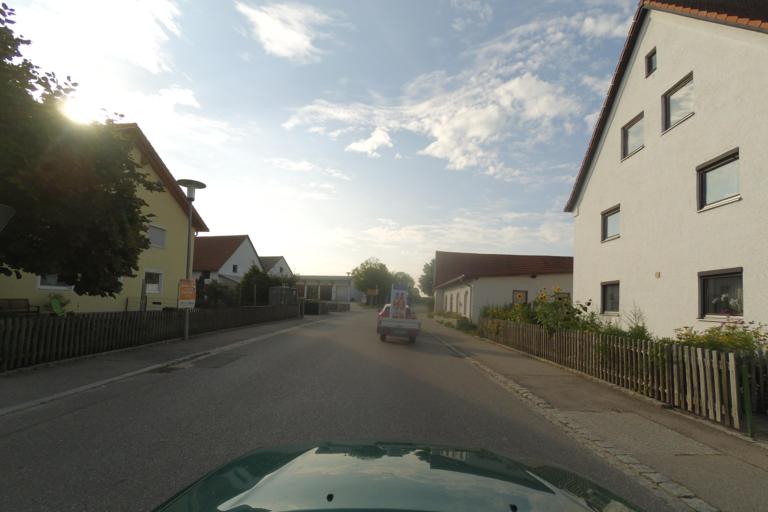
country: DE
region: Bavaria
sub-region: Upper Bavaria
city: Horgertshausen
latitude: 48.5497
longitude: 11.8652
